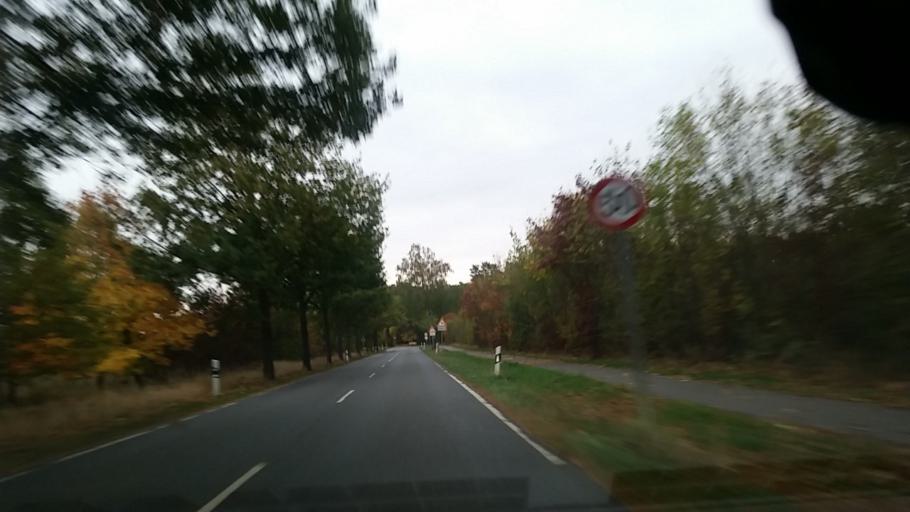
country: DE
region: Lower Saxony
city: Wolfsburg
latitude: 52.4638
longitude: 10.7833
